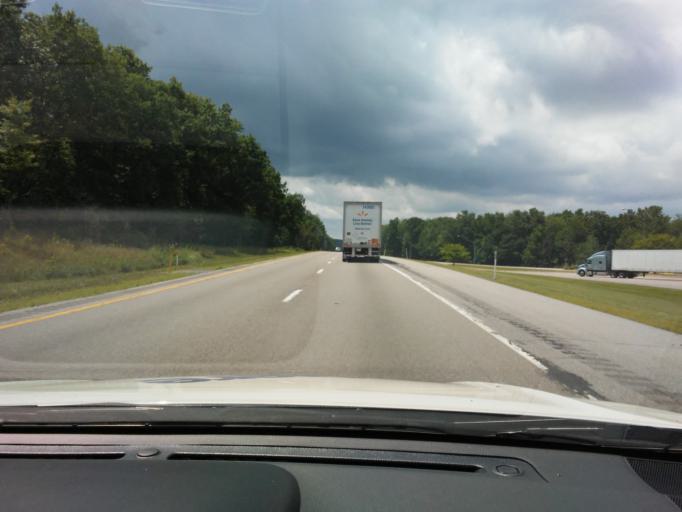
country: US
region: Pennsylvania
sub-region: Centre County
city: Milesburg
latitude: 41.0193
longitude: -77.9524
